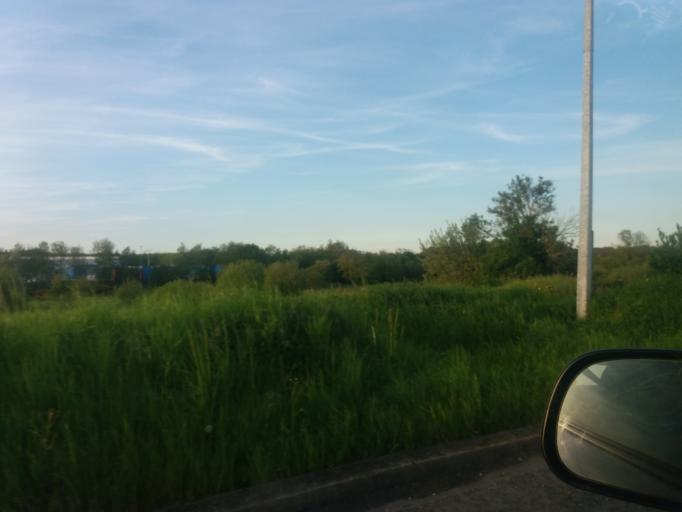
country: IE
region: Leinster
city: Donabate
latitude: 53.4894
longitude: -6.1910
